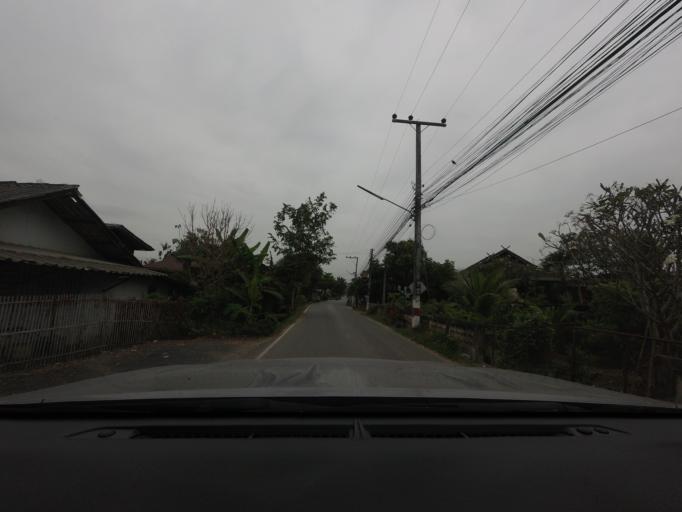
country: TH
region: Lamphun
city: Lamphun
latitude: 18.6299
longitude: 99.0148
